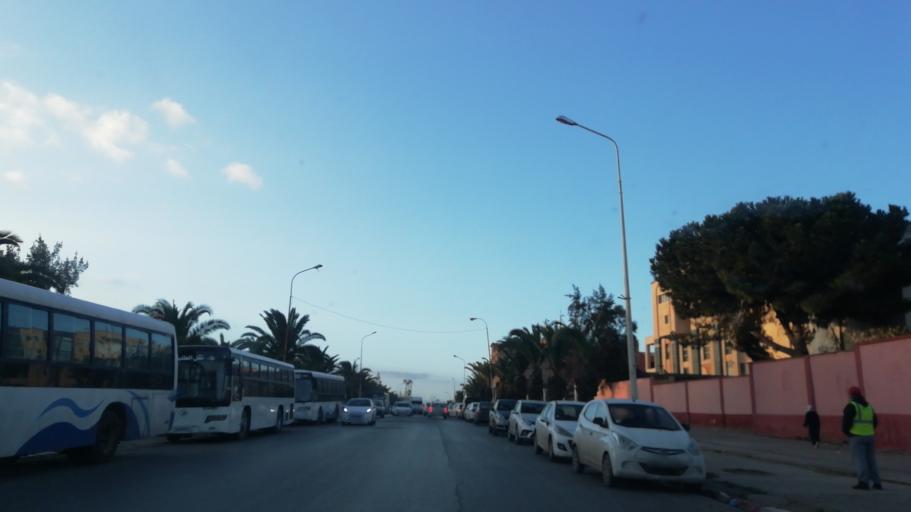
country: DZ
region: Oran
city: Oran
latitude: 35.6745
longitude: -0.6577
